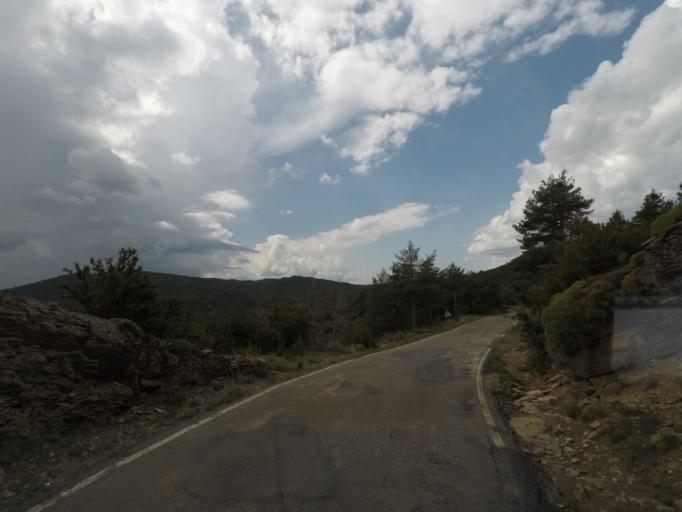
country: ES
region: Aragon
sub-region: Provincia de Huesca
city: Boltana
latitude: 42.3983
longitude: -0.0316
